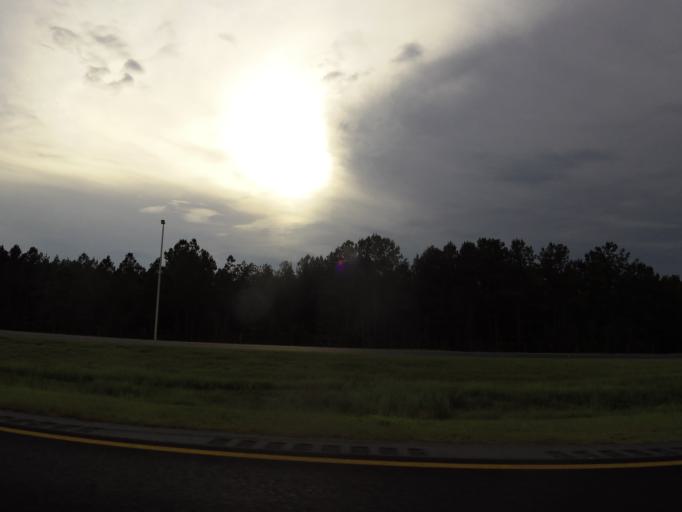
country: US
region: Florida
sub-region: Clay County
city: Middleburg
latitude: 30.1086
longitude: -81.8346
